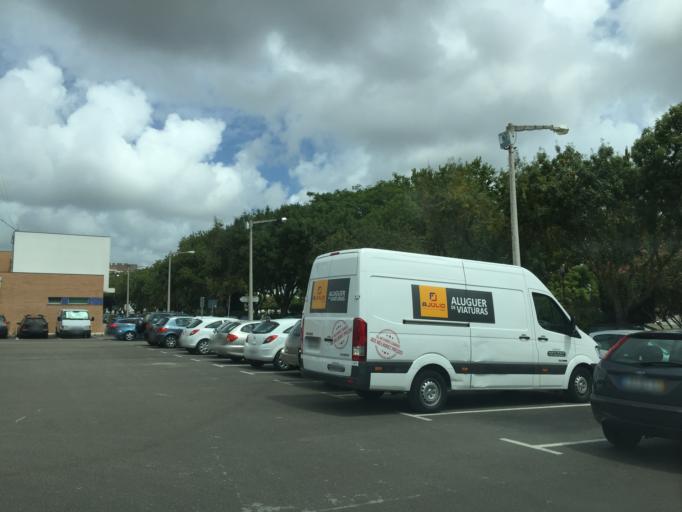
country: PT
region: Lisbon
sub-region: Torres Vedras
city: Torres Vedras
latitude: 39.0883
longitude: -9.2623
